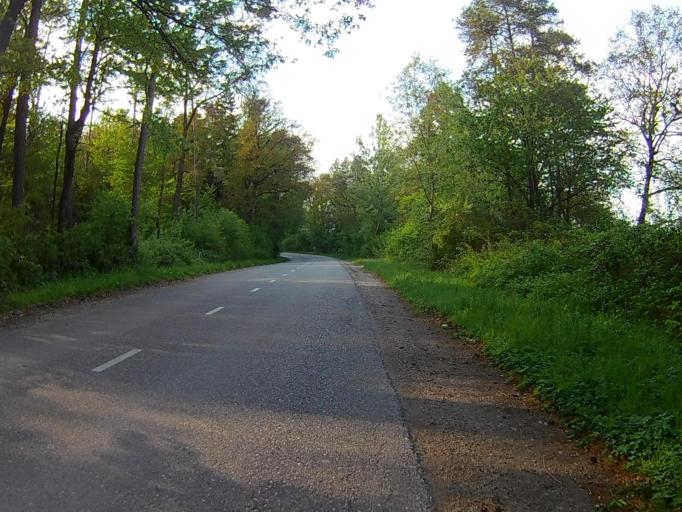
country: SI
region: Miklavz na Dravskem Polju
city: Miklavz na Dravskem Polju
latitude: 46.4731
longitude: 15.7098
